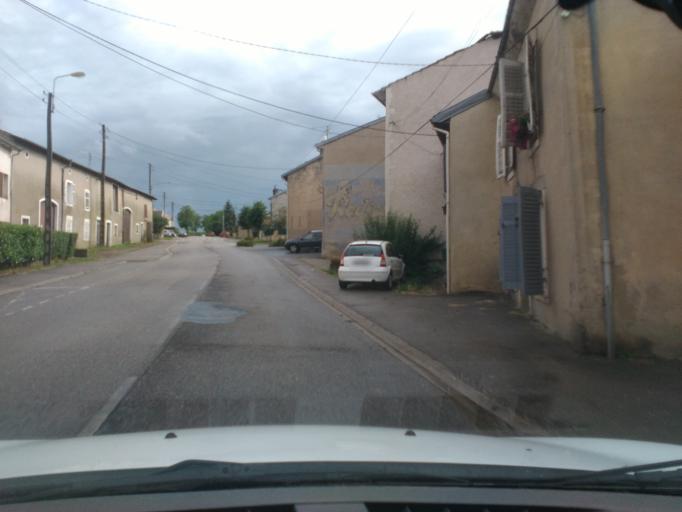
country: FR
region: Lorraine
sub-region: Departement de Meurthe-et-Moselle
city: Vezelise
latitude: 48.4672
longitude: 6.1347
